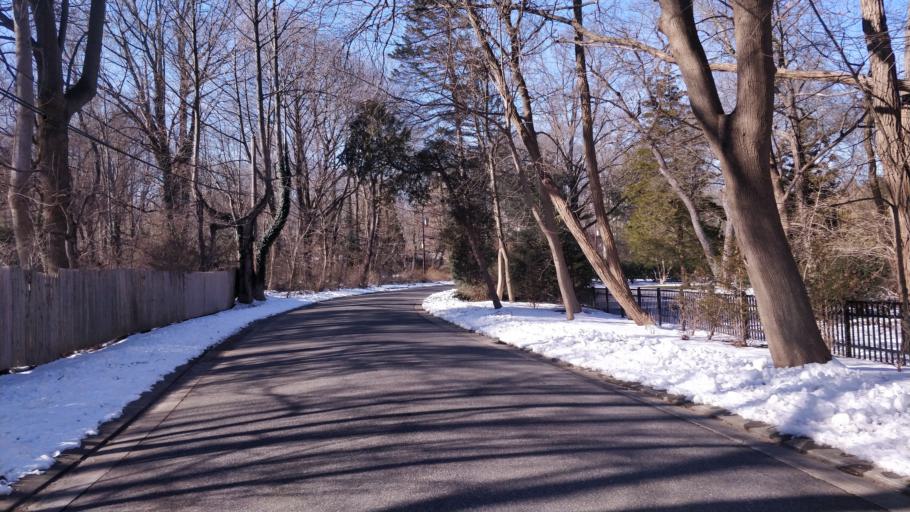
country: US
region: New York
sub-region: Nassau County
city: Old Brookville
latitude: 40.8493
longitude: -73.5930
